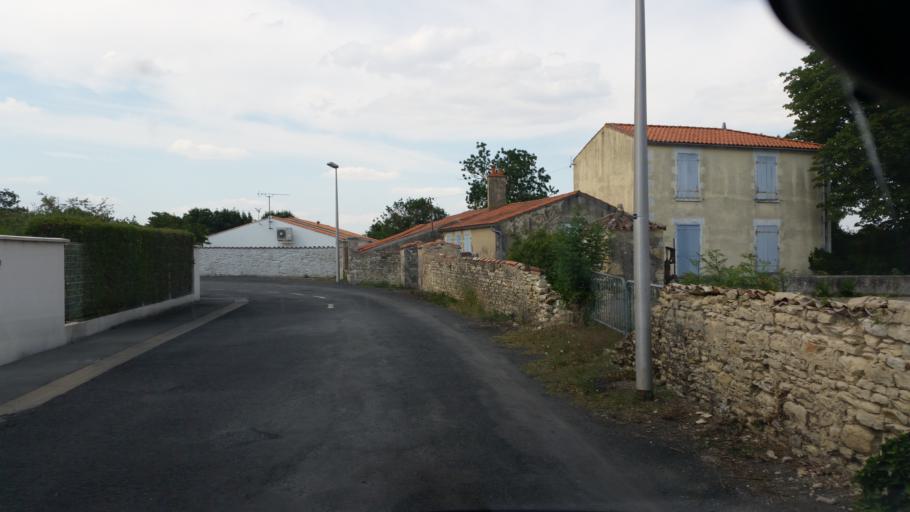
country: FR
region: Poitou-Charentes
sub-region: Departement de la Charente-Maritime
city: Marans
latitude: 46.3083
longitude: -0.9859
